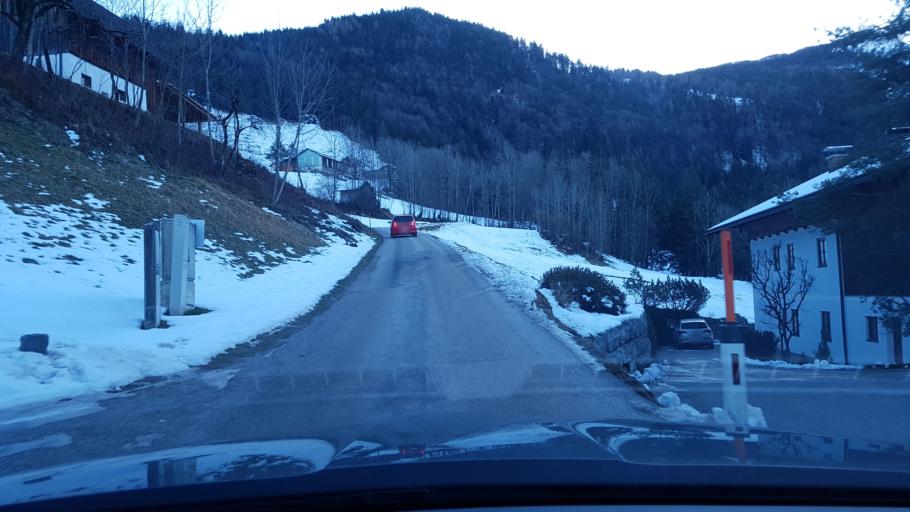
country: AT
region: Salzburg
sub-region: Politischer Bezirk Hallein
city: Scheffau am Tennengebirge
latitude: 47.6450
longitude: 13.2295
